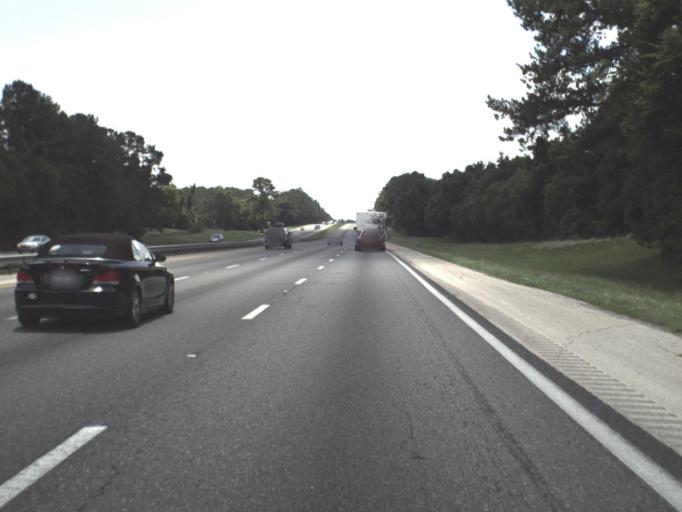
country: US
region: Florida
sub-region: Alachua County
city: Alachua
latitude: 29.7528
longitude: -82.4932
